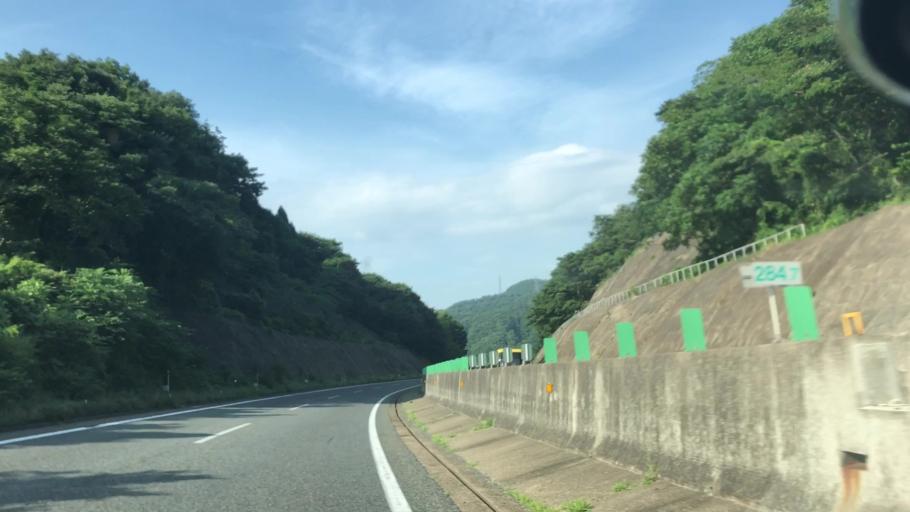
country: JP
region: Fukushima
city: Yanagawamachi-saiwaicho
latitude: 37.9188
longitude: 140.6039
